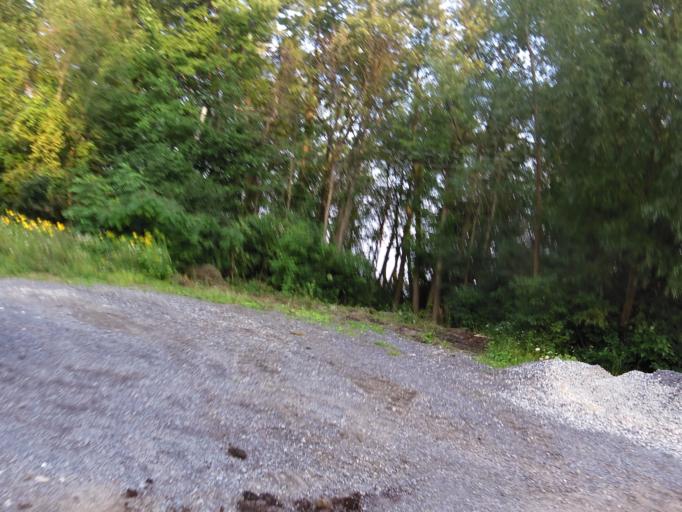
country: CA
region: Ontario
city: Bells Corners
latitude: 45.3809
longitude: -75.8221
